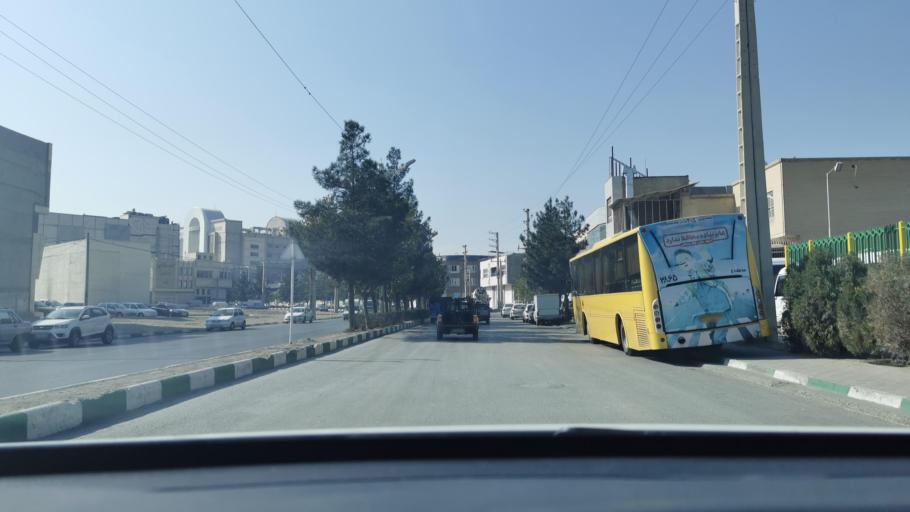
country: IR
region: Razavi Khorasan
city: Mashhad
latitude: 36.3488
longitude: 59.5977
